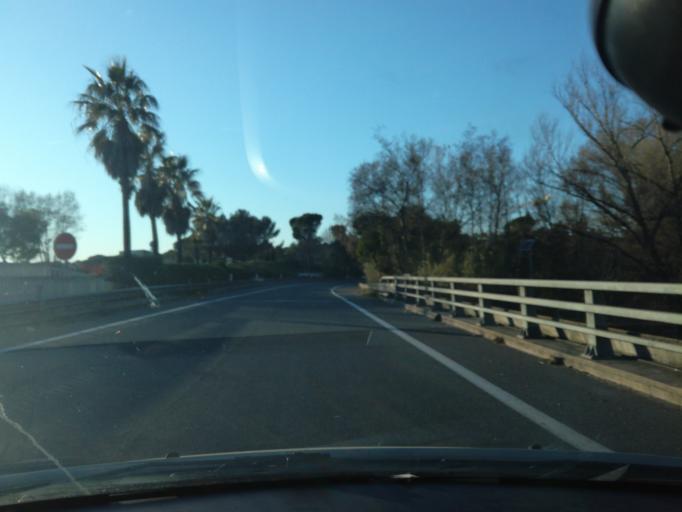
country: FR
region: Provence-Alpes-Cote d'Azur
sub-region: Departement du Var
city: Frejus
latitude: 43.4728
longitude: 6.7425
